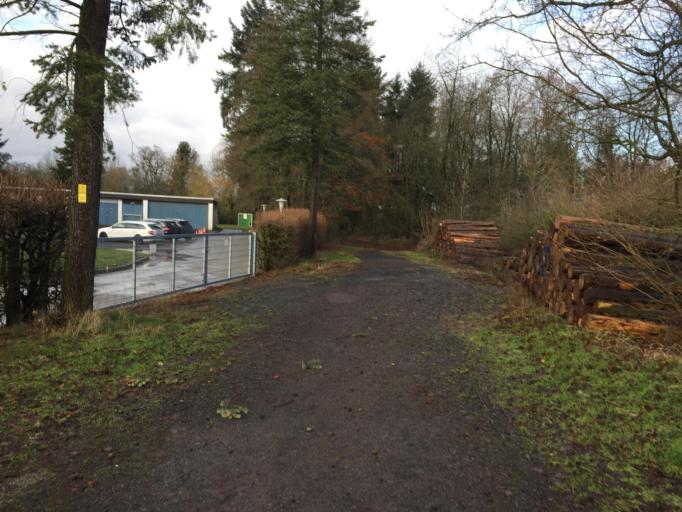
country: DE
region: Hesse
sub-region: Regierungsbezirk Giessen
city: Grunberg
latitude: 50.5882
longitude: 8.9767
